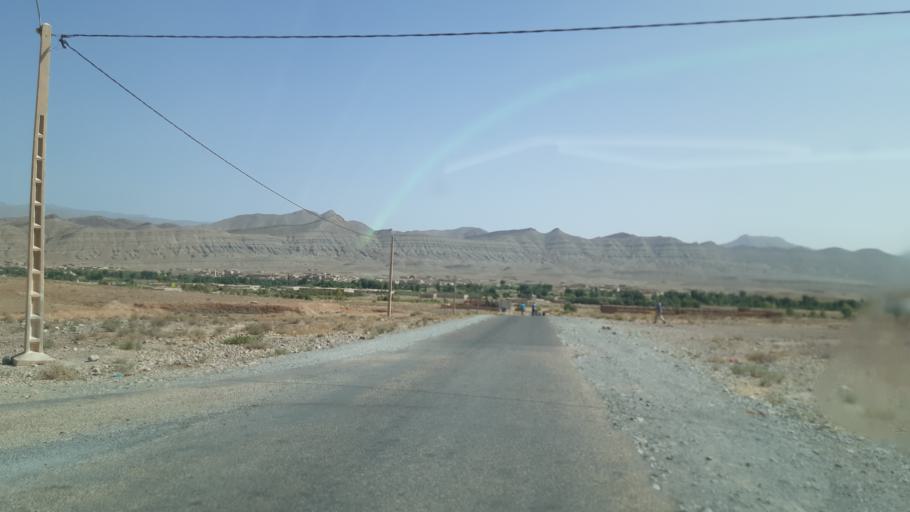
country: MA
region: Meknes-Tafilalet
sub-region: Errachidia
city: Amouguer
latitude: 32.2348
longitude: -4.7345
